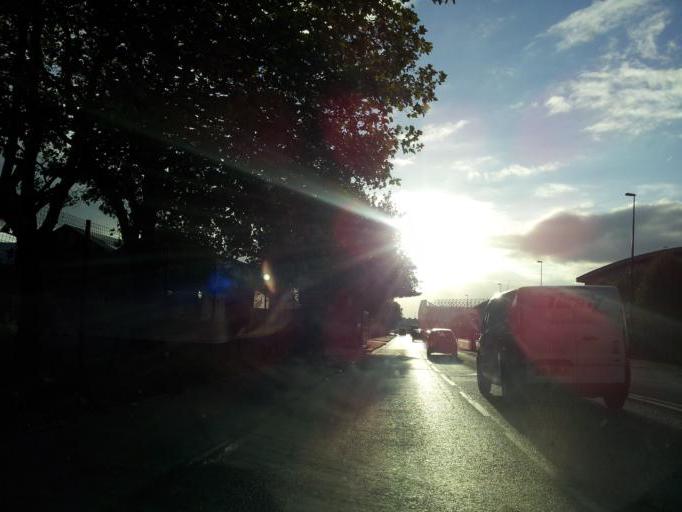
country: GB
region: England
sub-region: Trafford
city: Trafford Park
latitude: 53.4672
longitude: -2.3036
